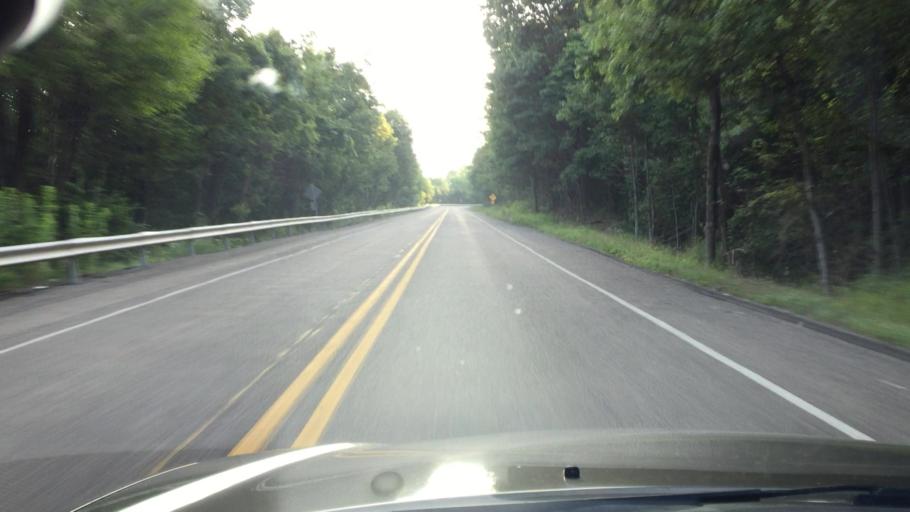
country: US
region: Pennsylvania
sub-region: Carbon County
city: Weatherly
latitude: 40.9258
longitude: -75.8856
